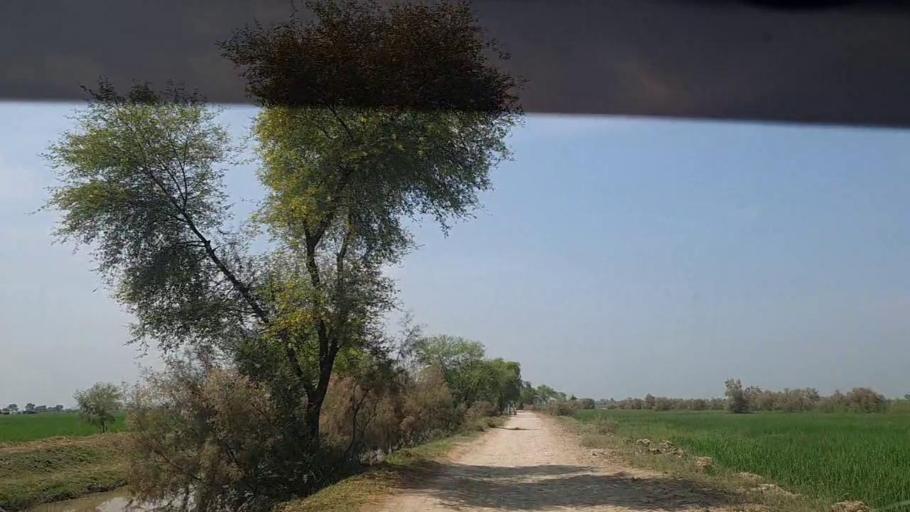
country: PK
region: Sindh
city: Thul
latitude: 28.1901
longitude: 68.7143
